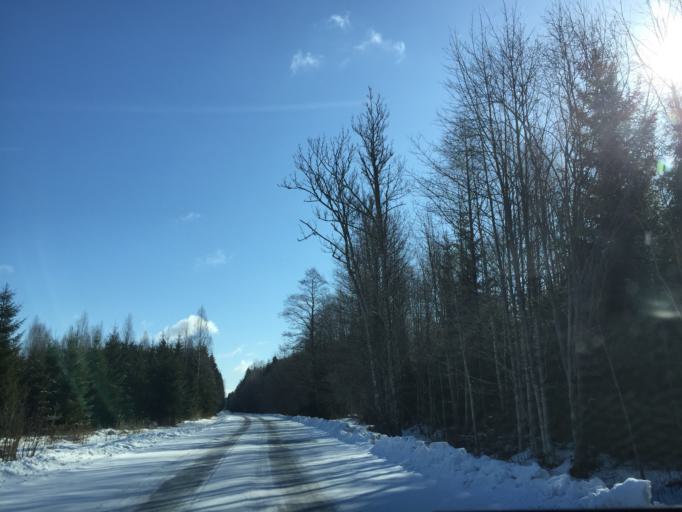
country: LV
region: Salacgrivas
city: Ainazi
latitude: 57.9974
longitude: 24.5427
